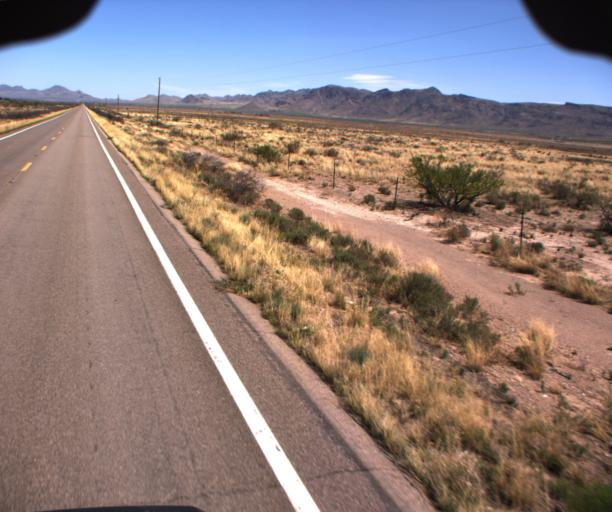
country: US
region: Arizona
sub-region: Cochise County
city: Douglas
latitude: 31.7734
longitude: -109.0752
